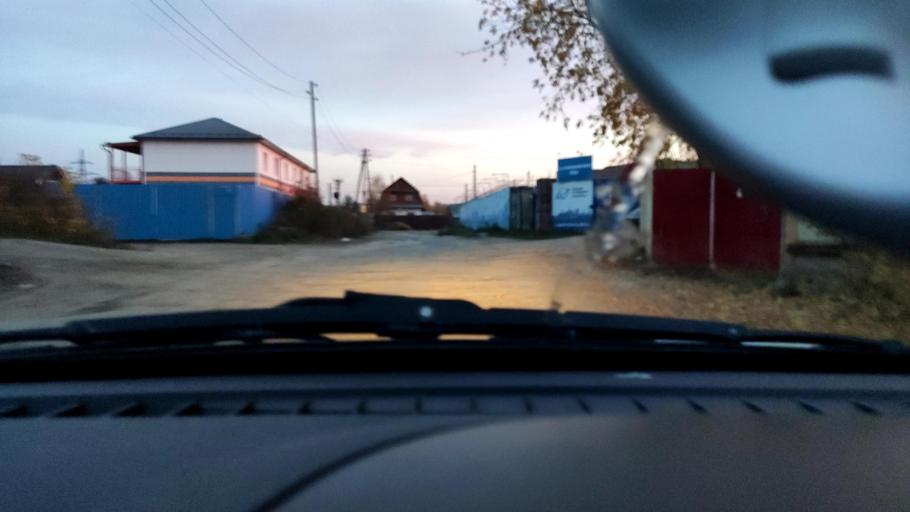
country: RU
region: Perm
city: Kondratovo
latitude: 58.0075
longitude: 56.0974
